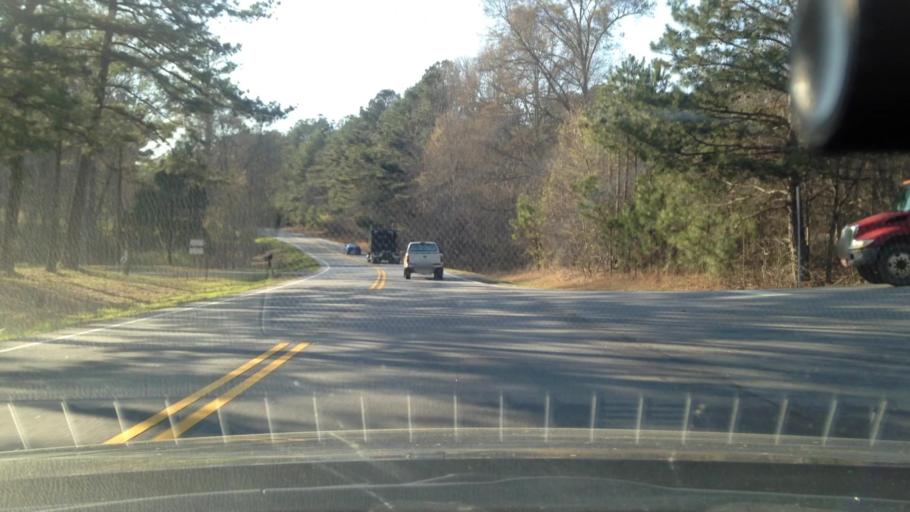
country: US
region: Georgia
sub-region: Fayette County
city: Peachtree City
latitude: 33.3385
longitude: -84.6520
